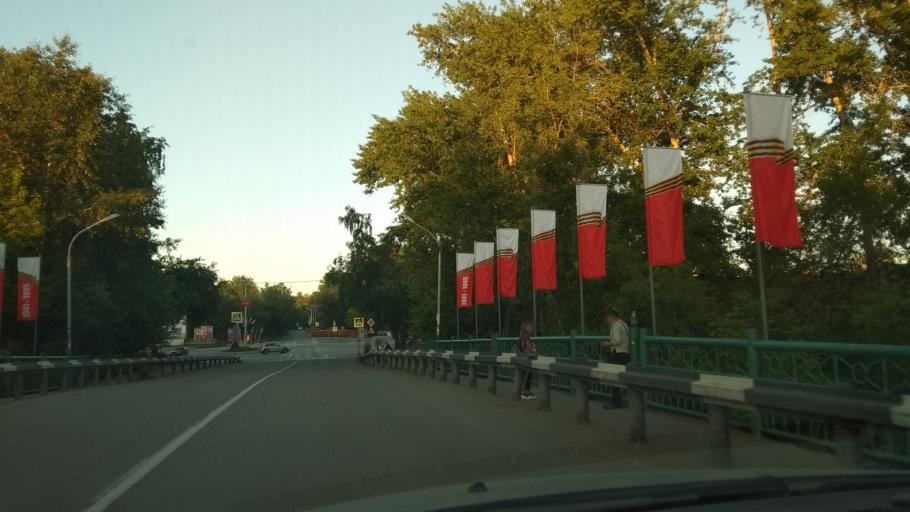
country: RU
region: Sverdlovsk
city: Sredneuralsk
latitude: 56.9888
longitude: 60.4613
